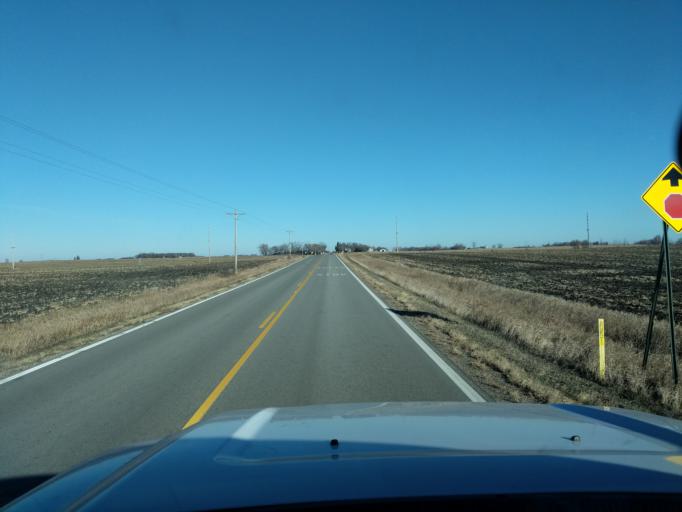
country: US
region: Minnesota
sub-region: Yellow Medicine County
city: Granite Falls
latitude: 44.7866
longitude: -95.4017
